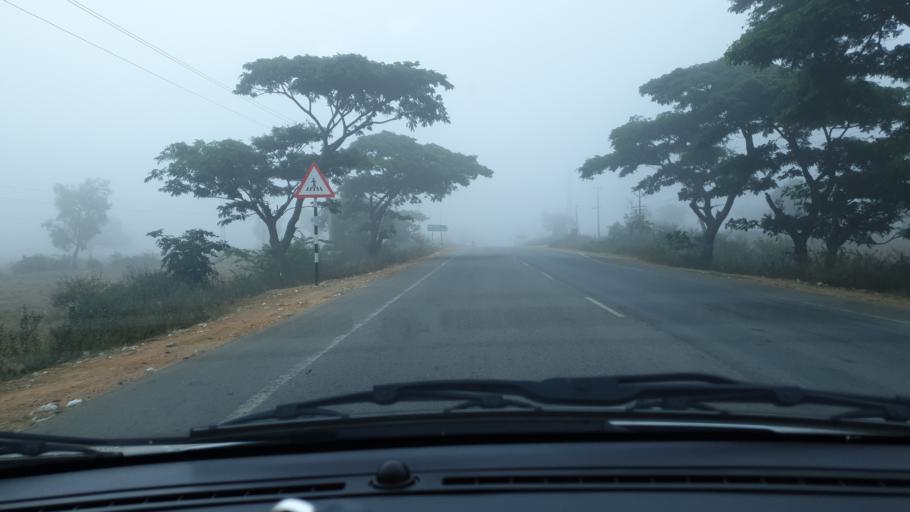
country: IN
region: Telangana
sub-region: Mahbubnagar
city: Nagar Karnul
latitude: 16.6640
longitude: 78.5640
